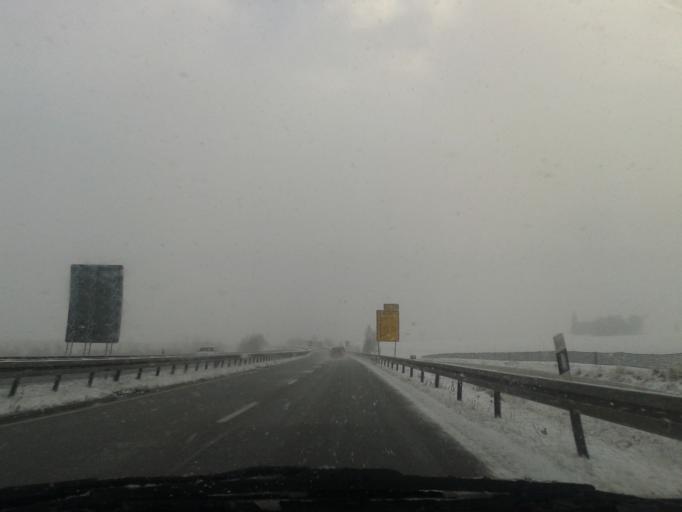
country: DE
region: Saxony
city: Grossschweidnitz
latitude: 51.0853
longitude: 14.6467
